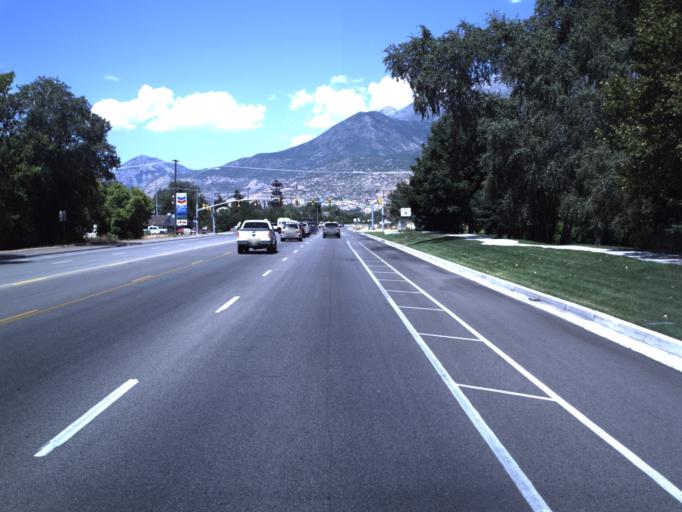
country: US
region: Utah
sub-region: Utah County
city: Orem
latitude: 40.2812
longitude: -111.6581
